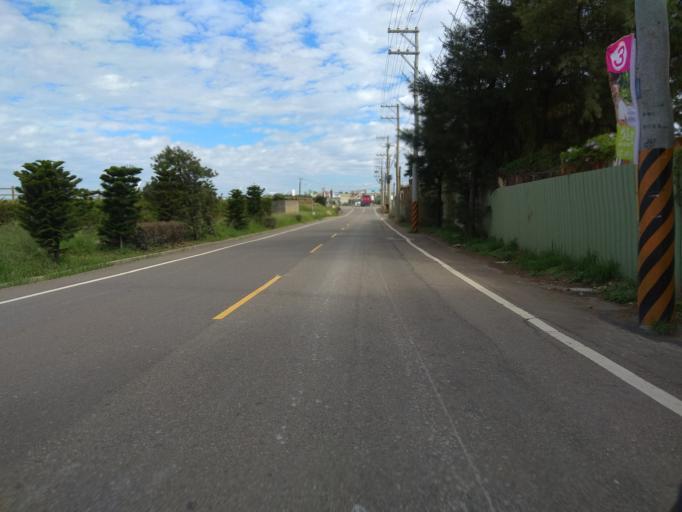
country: TW
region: Taiwan
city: Taoyuan City
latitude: 25.0537
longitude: 121.0981
